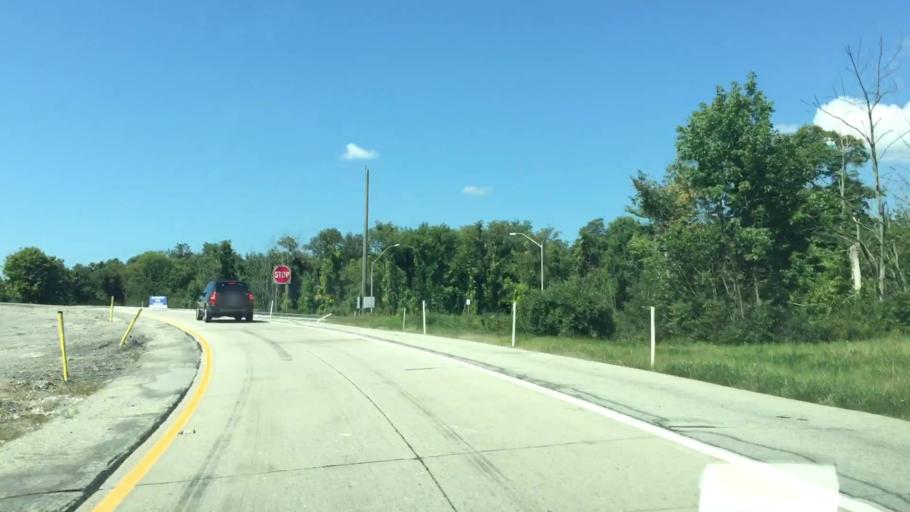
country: US
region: Pennsylvania
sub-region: Allegheny County
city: Enlow
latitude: 40.4731
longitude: -80.2216
